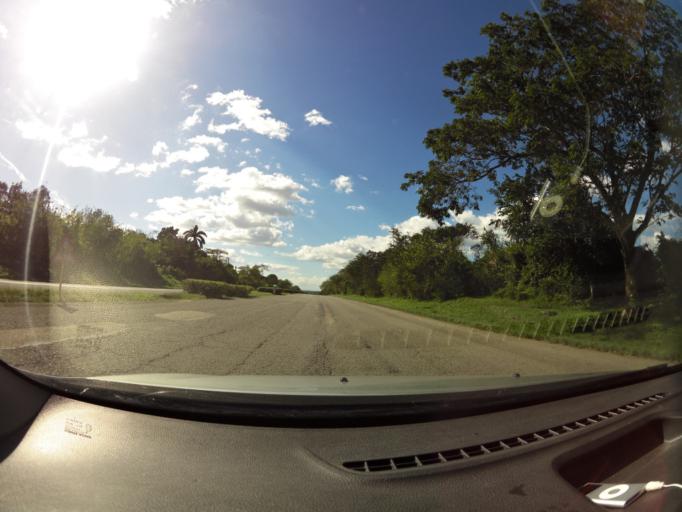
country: CU
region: Santiago de Cuba
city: San Luis
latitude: 20.1725
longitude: -75.7993
